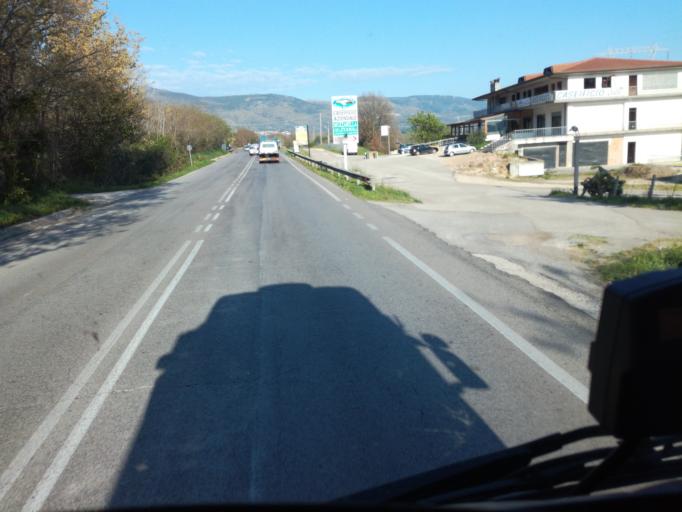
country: IT
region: Latium
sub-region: Provincia di Latina
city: Prossedi
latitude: 41.5078
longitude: 13.2540
